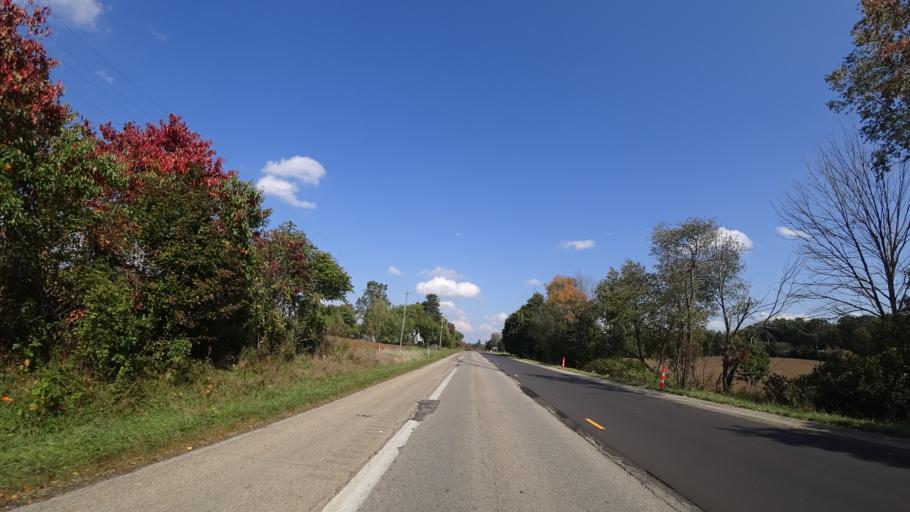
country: US
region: Michigan
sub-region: Calhoun County
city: Homer
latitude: 42.1228
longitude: -84.9378
